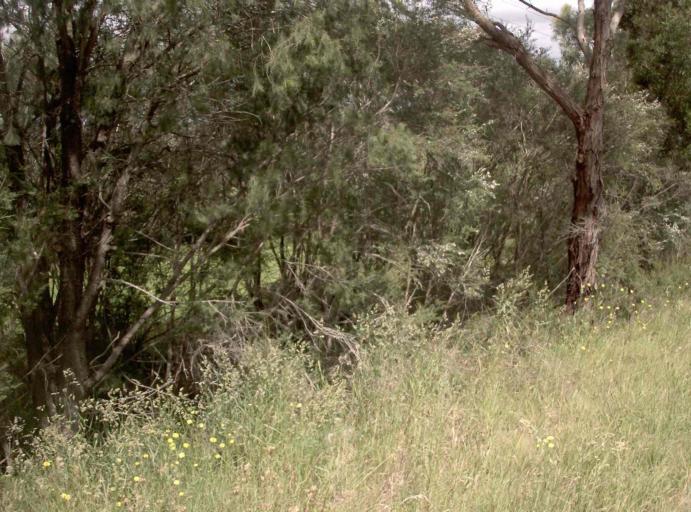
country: AU
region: Victoria
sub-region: Latrobe
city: Moe
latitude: -38.0829
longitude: 146.1947
